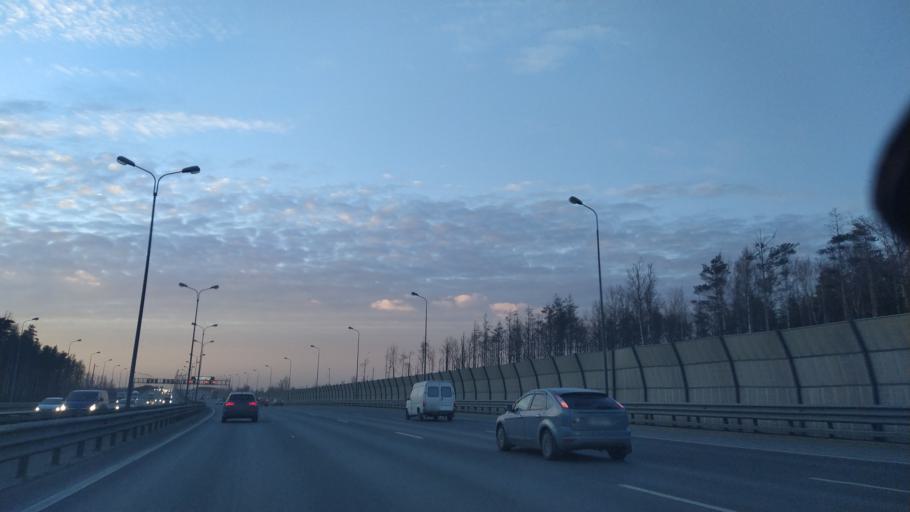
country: RU
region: St.-Petersburg
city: Krasnogvargeisky
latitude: 59.9734
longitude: 30.5436
